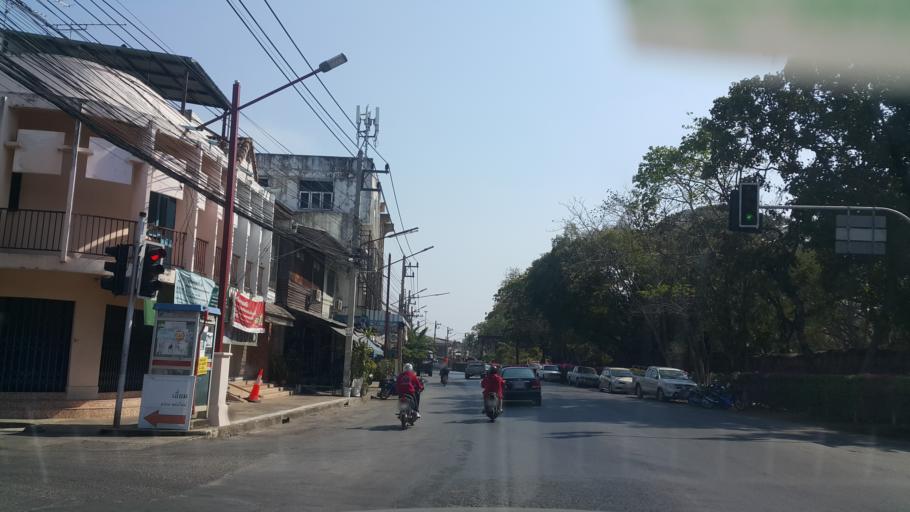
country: TH
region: Nakhon Ratchasima
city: Phimai
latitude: 15.2226
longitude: 102.4944
